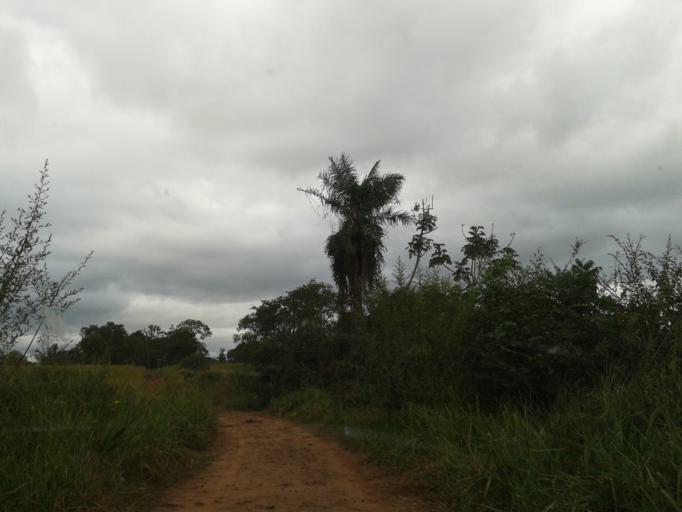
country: BR
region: Minas Gerais
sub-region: Campina Verde
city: Campina Verde
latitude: -19.4878
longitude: -49.6284
